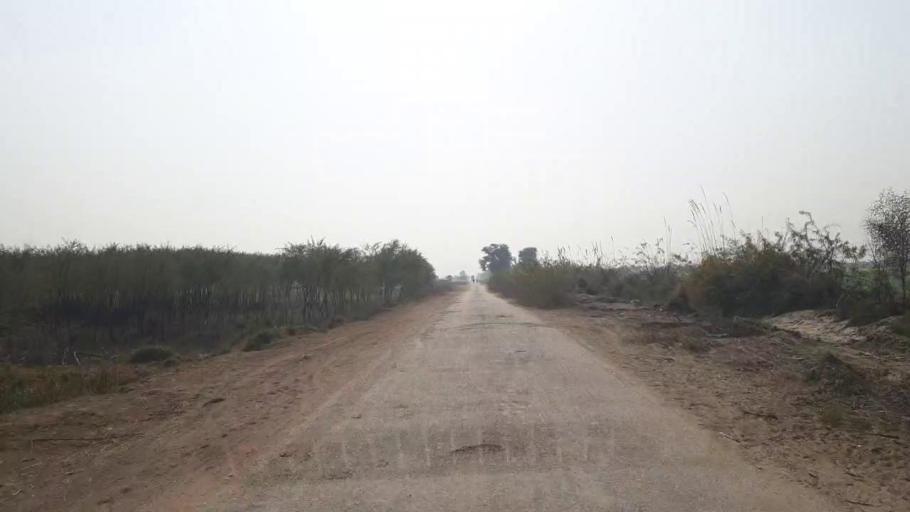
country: PK
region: Sindh
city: Hala
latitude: 25.9165
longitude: 68.4459
